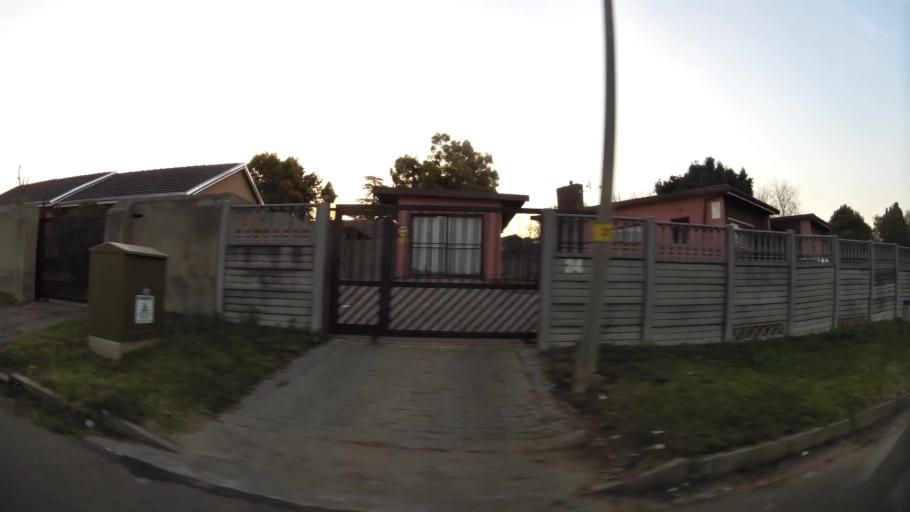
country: ZA
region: Gauteng
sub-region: Ekurhuleni Metropolitan Municipality
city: Tembisa
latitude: -26.0612
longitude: 28.2391
